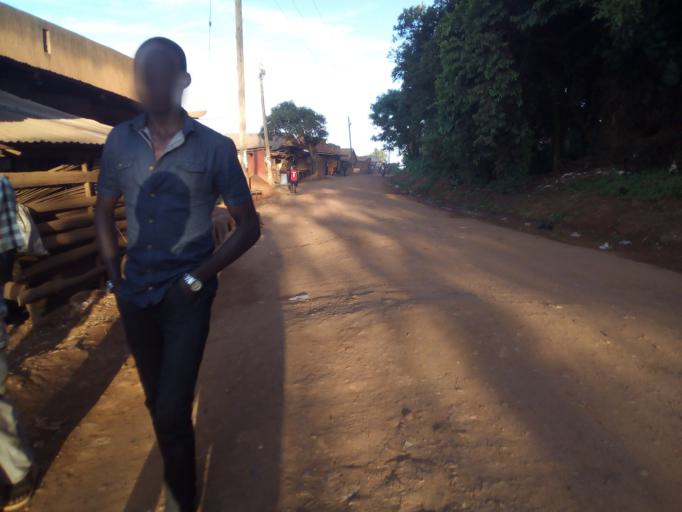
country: UG
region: Central Region
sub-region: Wakiso District
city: Kajansi
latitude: 0.2466
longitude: 32.5758
